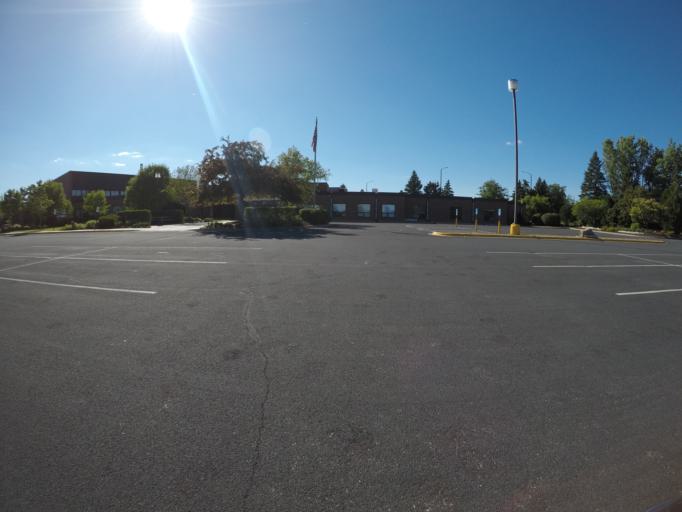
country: US
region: Minnesota
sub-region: Hennepin County
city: Maple Grove
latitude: 45.0850
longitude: -93.4293
